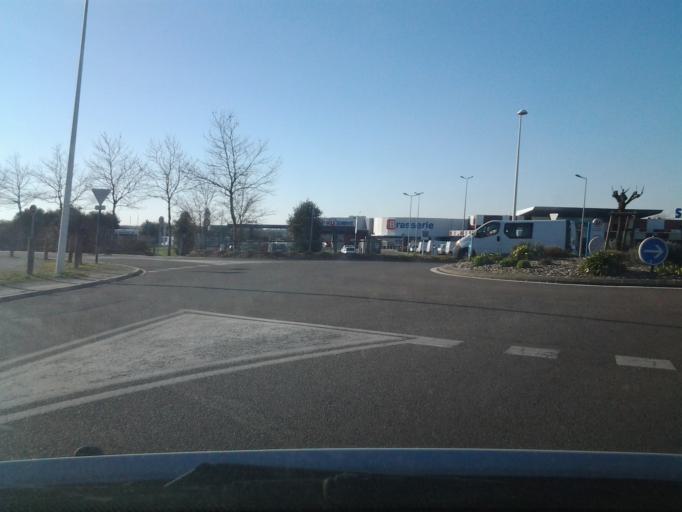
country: FR
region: Pays de la Loire
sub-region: Departement de la Vendee
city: Olonne-sur-Mer
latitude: 46.5424
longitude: -1.7710
